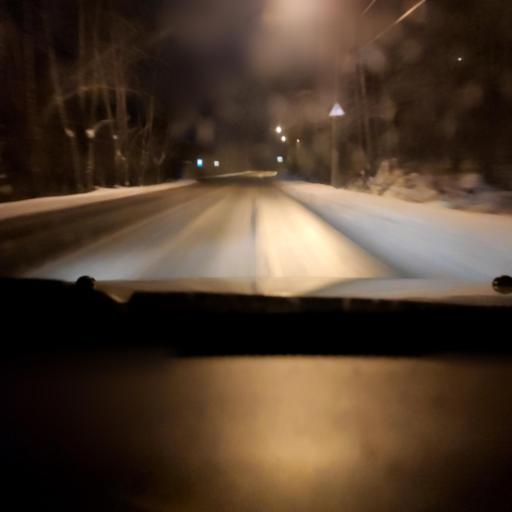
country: RU
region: Perm
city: Perm
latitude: 58.0770
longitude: 56.3497
